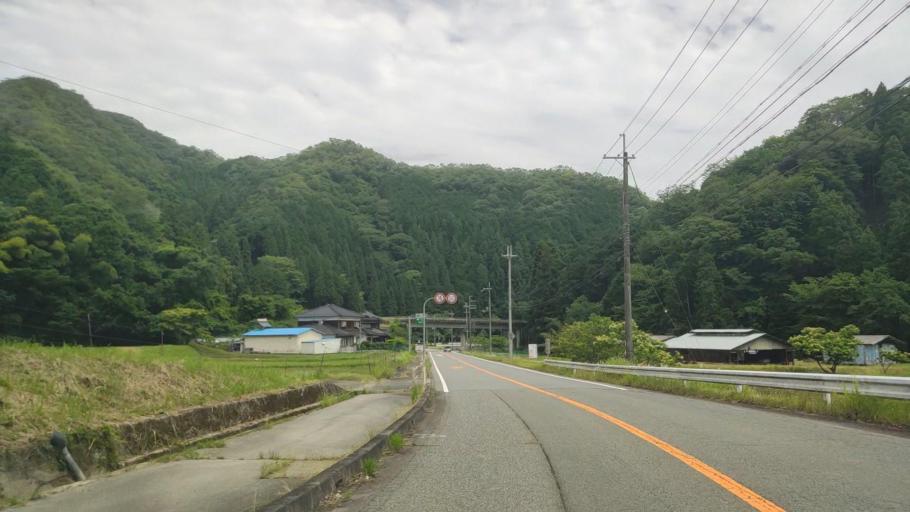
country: JP
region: Hyogo
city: Yamazakicho-nakabirose
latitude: 35.0722
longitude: 134.3576
